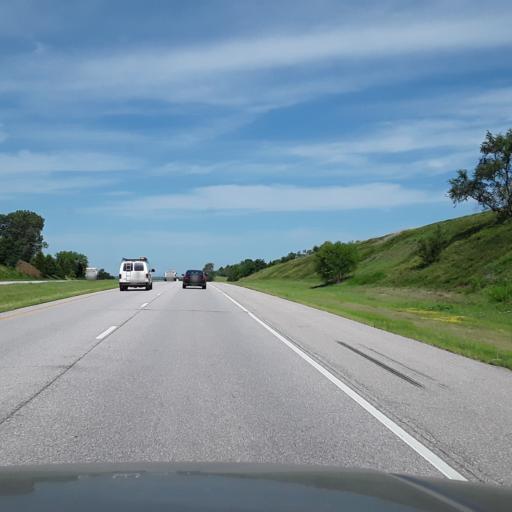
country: US
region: Nebraska
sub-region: Lancaster County
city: Lincoln
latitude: 40.8767
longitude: -96.7368
